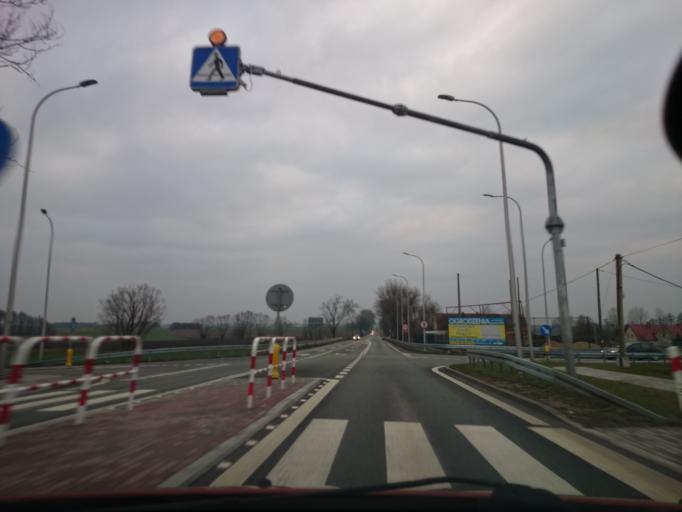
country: PL
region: Opole Voivodeship
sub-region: Powiat nyski
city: Pakoslawice
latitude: 50.5441
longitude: 17.3710
